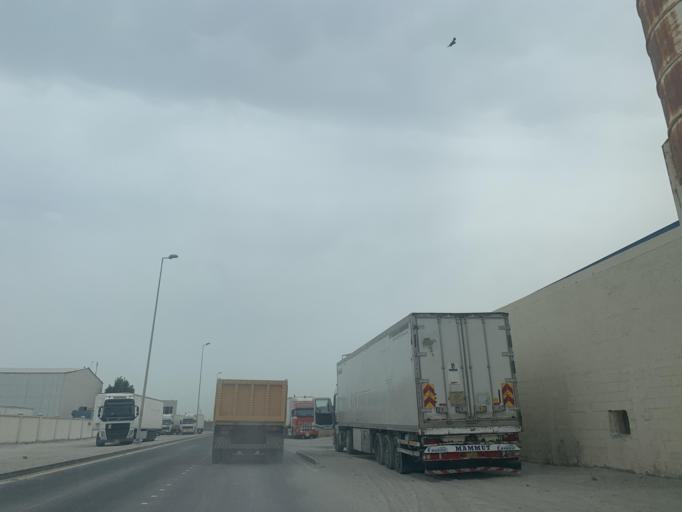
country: BH
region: Muharraq
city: Al Hadd
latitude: 26.2062
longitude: 50.6627
